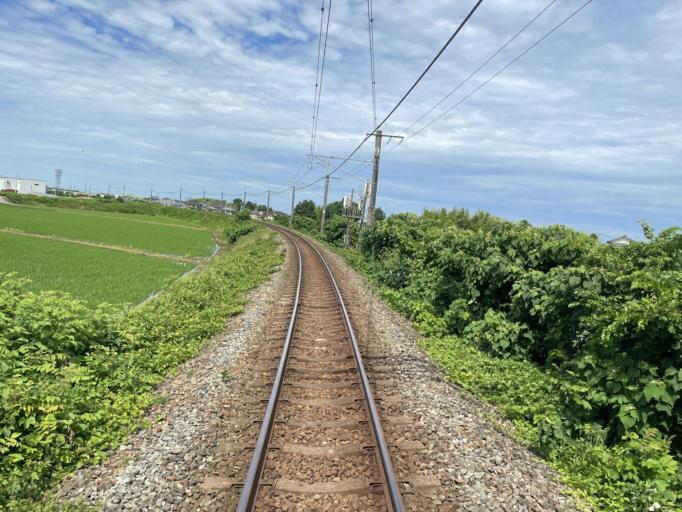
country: JP
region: Niigata
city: Shibata
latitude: 37.9508
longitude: 139.2646
